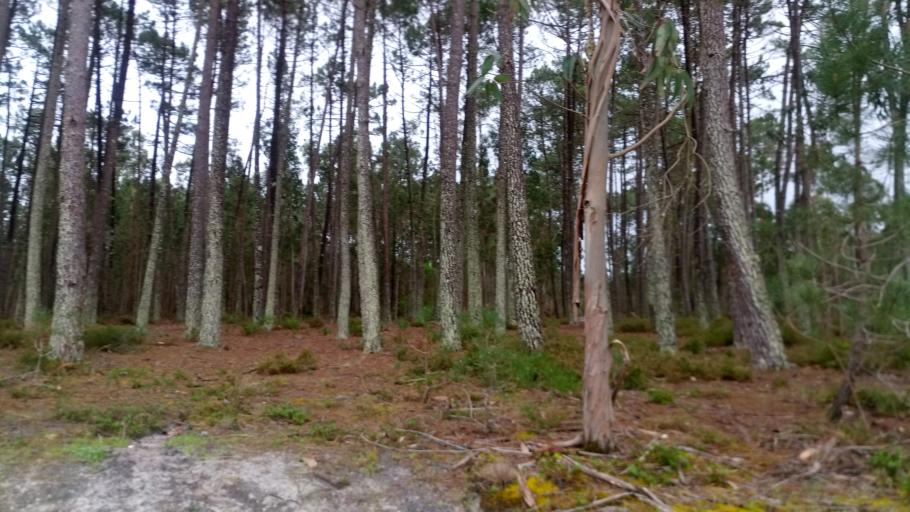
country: PT
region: Leiria
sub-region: Caldas da Rainha
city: Caldas da Rainha
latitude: 39.4549
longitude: -9.1549
